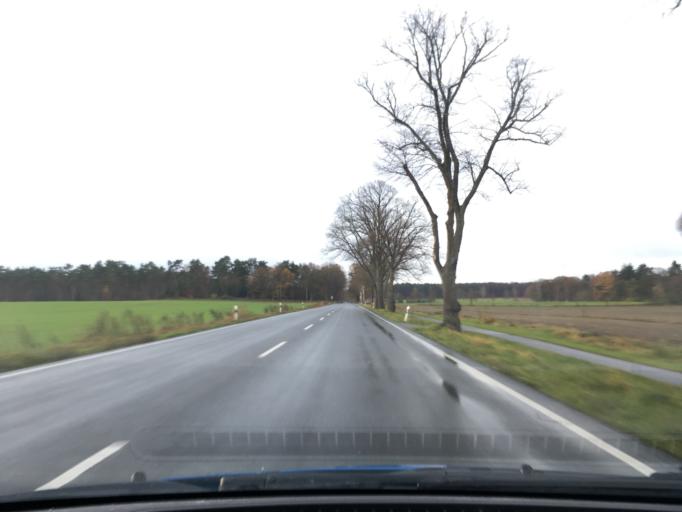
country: DE
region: Lower Saxony
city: Embsen
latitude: 53.1844
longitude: 10.3260
